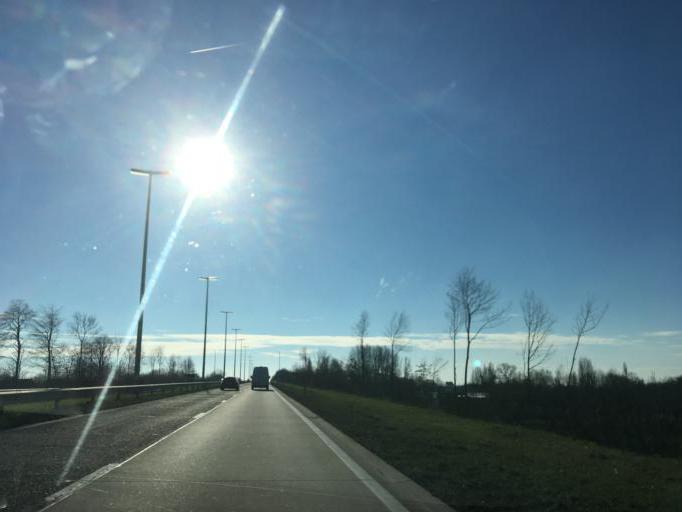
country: BE
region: Flanders
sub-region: Provincie Oost-Vlaanderen
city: Aalter
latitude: 51.0971
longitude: 3.4379
